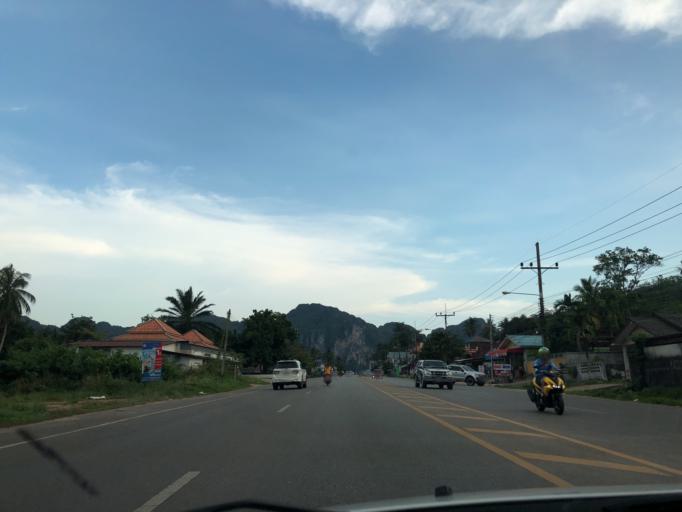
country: TH
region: Phangnga
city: Ban Ao Nang
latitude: 8.0491
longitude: 98.8380
